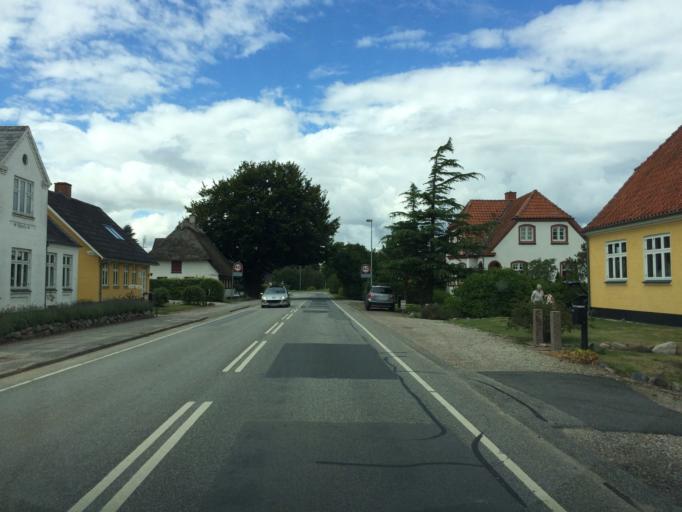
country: DK
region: South Denmark
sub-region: Assens Kommune
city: Harby
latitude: 55.1491
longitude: 10.1520
